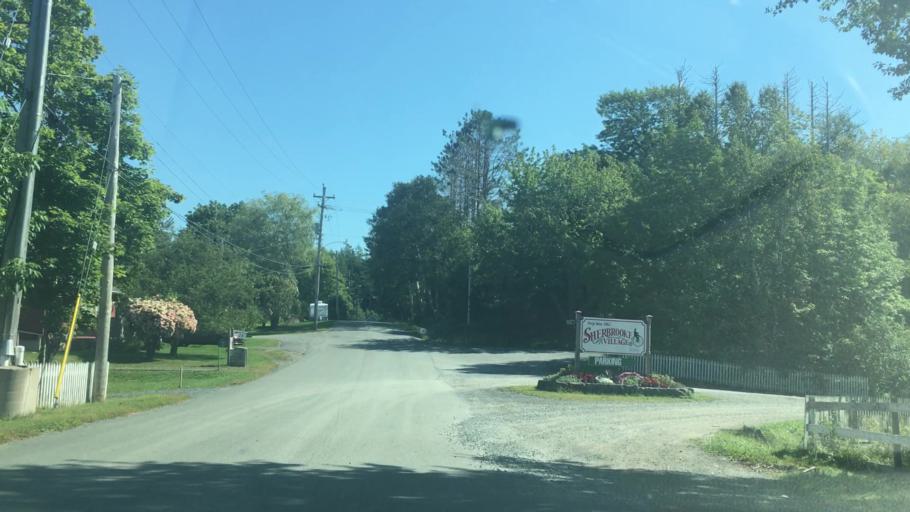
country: CA
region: Nova Scotia
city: Antigonish
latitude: 45.1408
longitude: -61.9832
